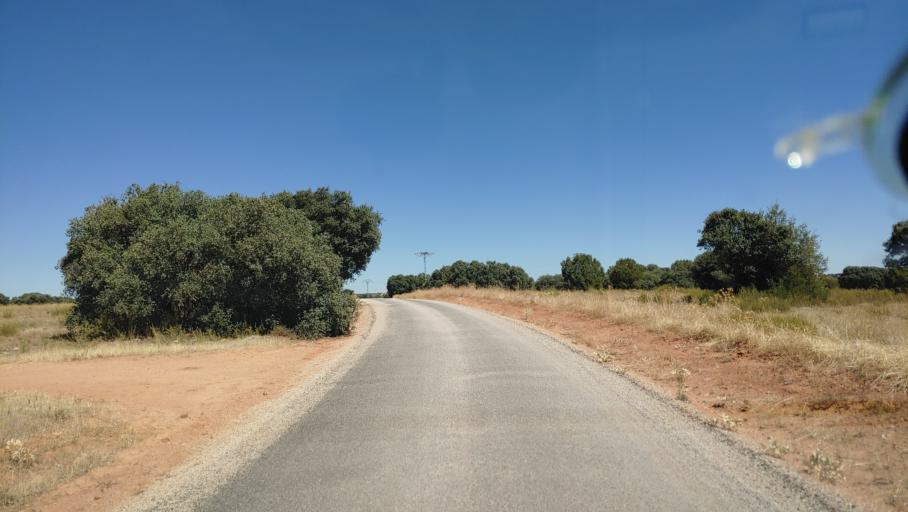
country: ES
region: Castille-La Mancha
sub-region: Provincia de Albacete
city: Ossa de Montiel
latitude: 38.9209
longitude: -2.7950
